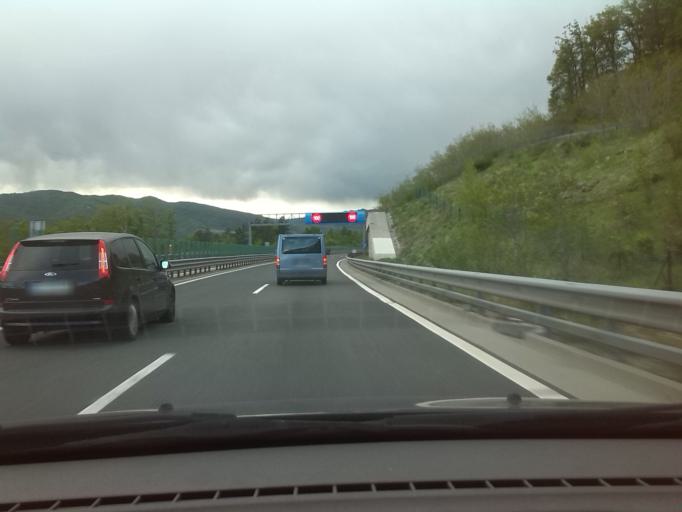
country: SI
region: Vipava
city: Vipava
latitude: 45.7799
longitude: 14.0153
